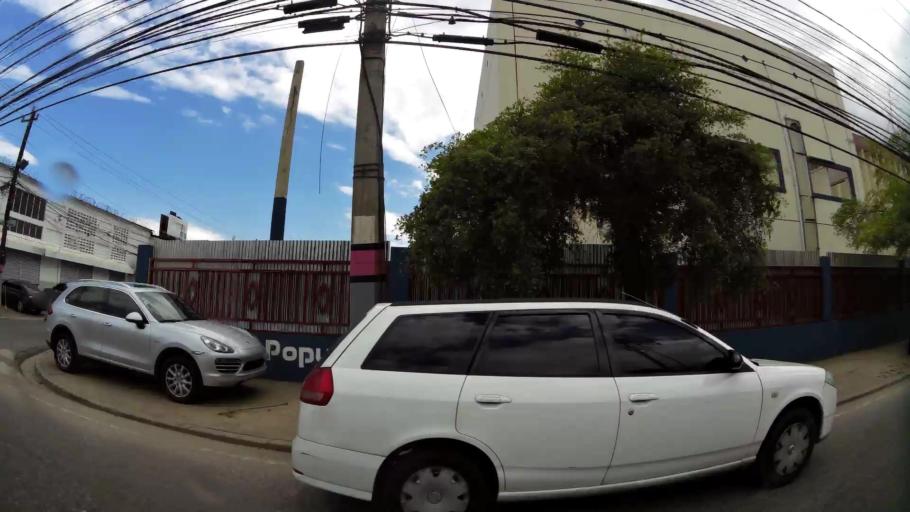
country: DO
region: Nacional
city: La Agustina
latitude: 18.4839
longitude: -69.9271
